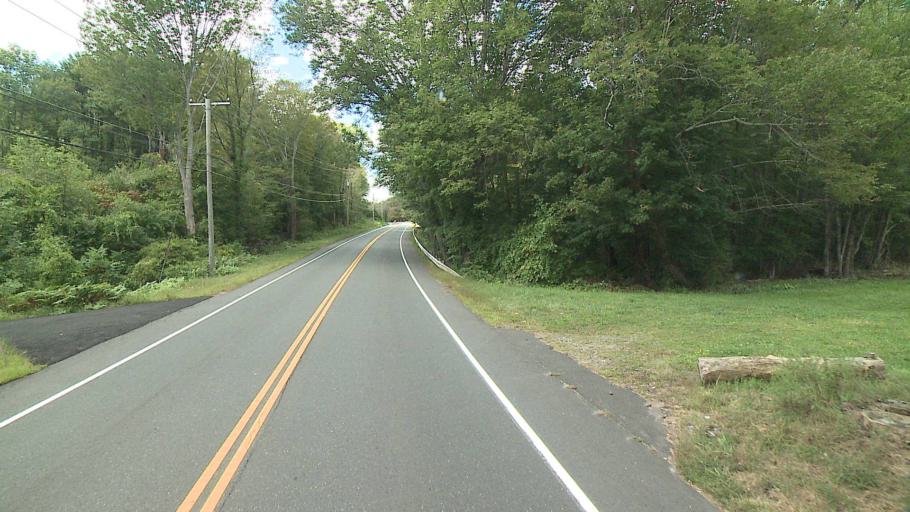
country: US
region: Connecticut
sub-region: Tolland County
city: Coventry Lake
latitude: 41.7994
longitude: -72.3512
